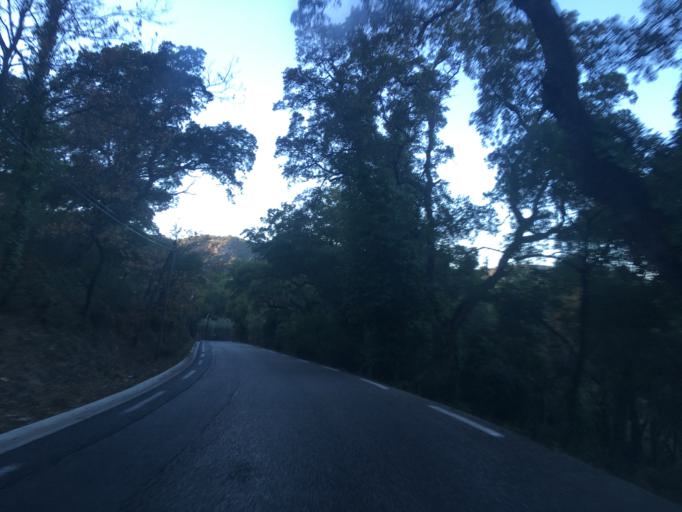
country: FR
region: Provence-Alpes-Cote d'Azur
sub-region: Departement du Var
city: Le Plan-de-la-Tour
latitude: 43.3146
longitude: 6.5449
